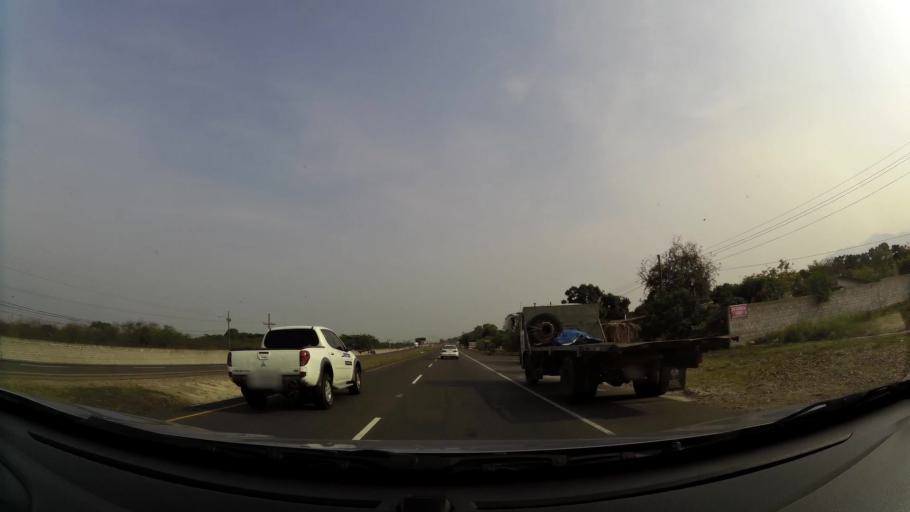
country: HN
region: La Paz
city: Yarumela
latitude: 14.3729
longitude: -87.6062
